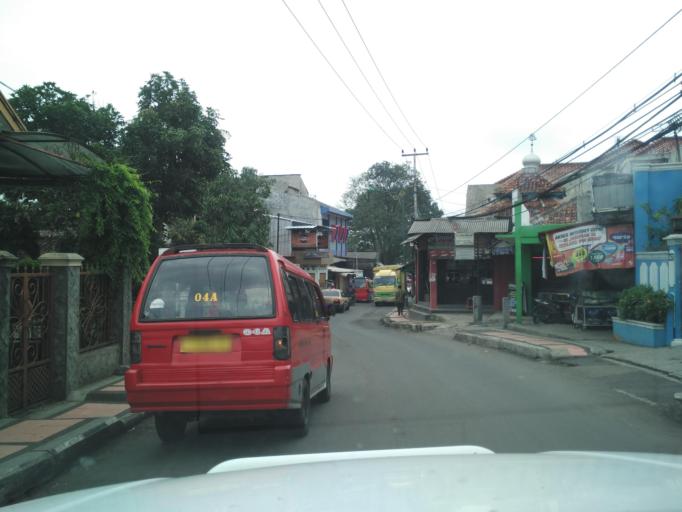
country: ID
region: West Java
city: Ciranjang-hilir
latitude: -6.8261
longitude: 107.1329
